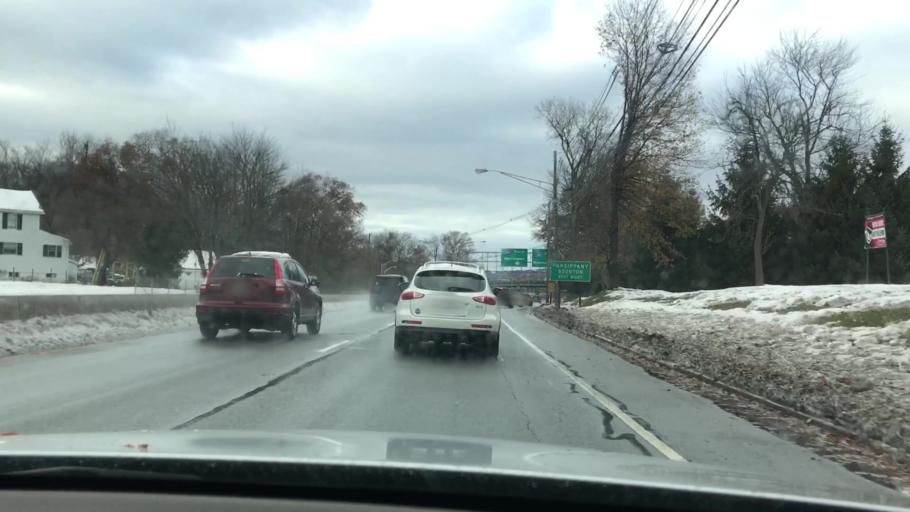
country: US
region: New Jersey
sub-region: Morris County
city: Parsippany
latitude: 40.8302
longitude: -74.4342
